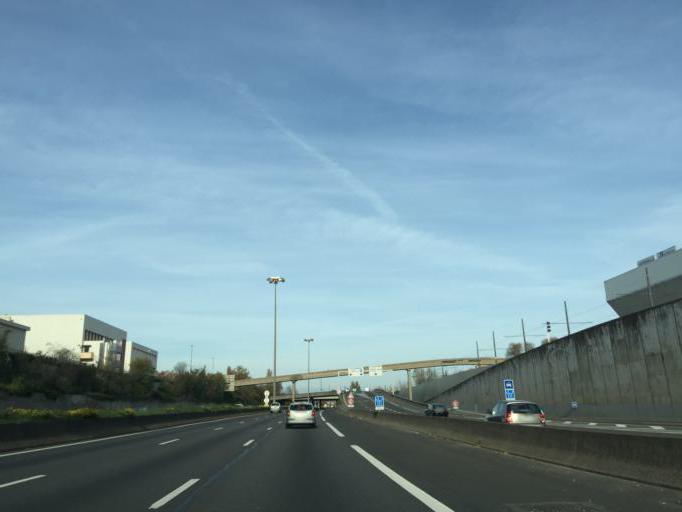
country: FR
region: Rhone-Alpes
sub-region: Departement du Rhone
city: Vaulx-en-Velin
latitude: 45.7653
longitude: 4.9072
